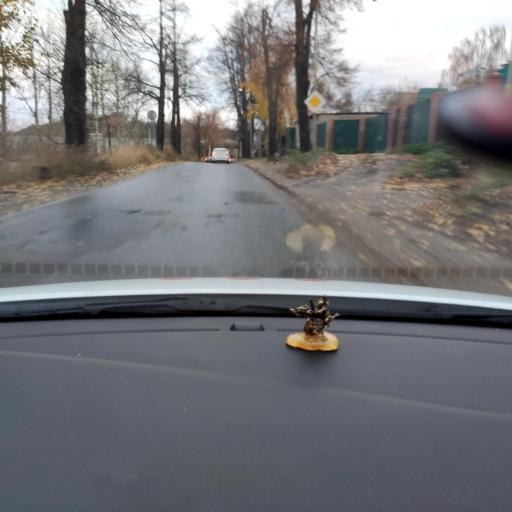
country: RU
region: Tatarstan
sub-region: Gorod Kazan'
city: Kazan
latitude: 55.7280
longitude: 49.1581
